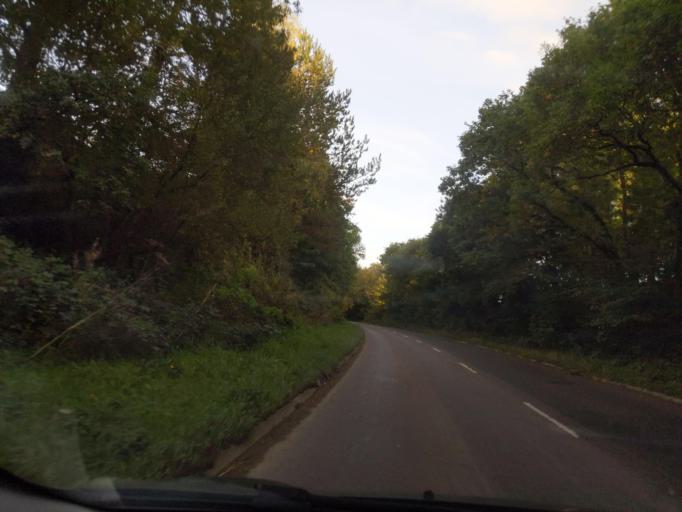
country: GB
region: England
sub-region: Devon
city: Bovey Tracey
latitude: 50.5852
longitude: -3.6790
